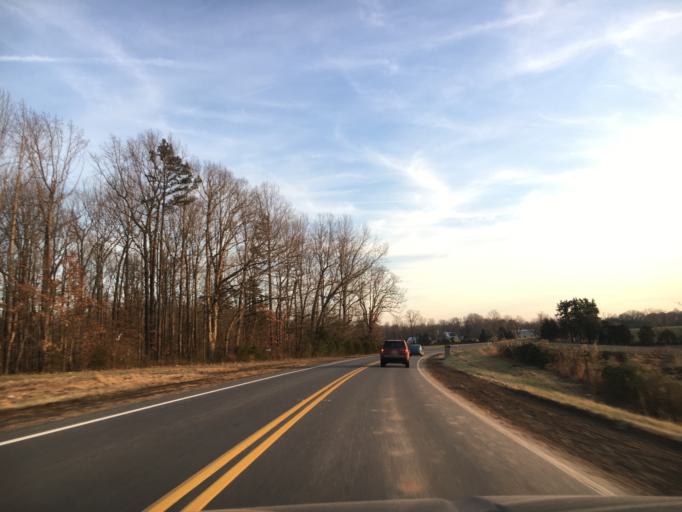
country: US
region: Virginia
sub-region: Louisa County
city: Louisa
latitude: 38.1644
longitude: -77.9318
